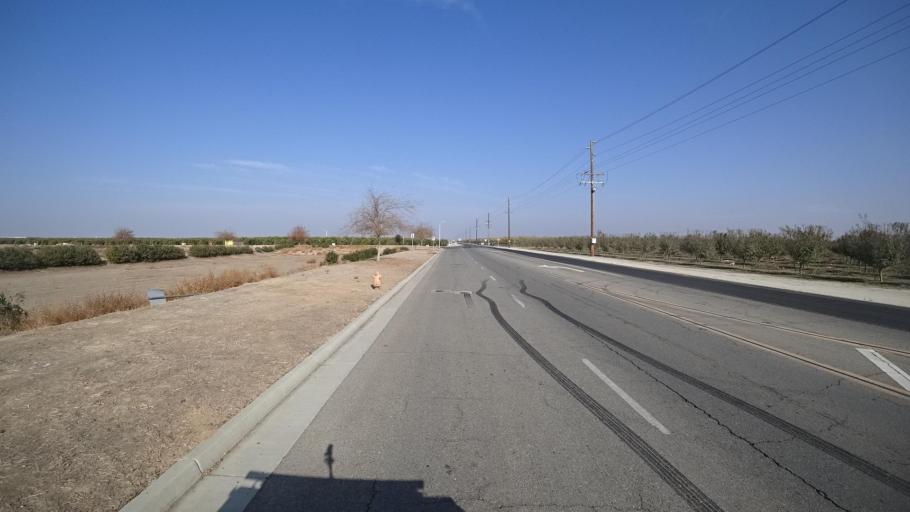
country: US
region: California
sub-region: Kern County
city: Delano
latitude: 35.7313
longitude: -119.2232
